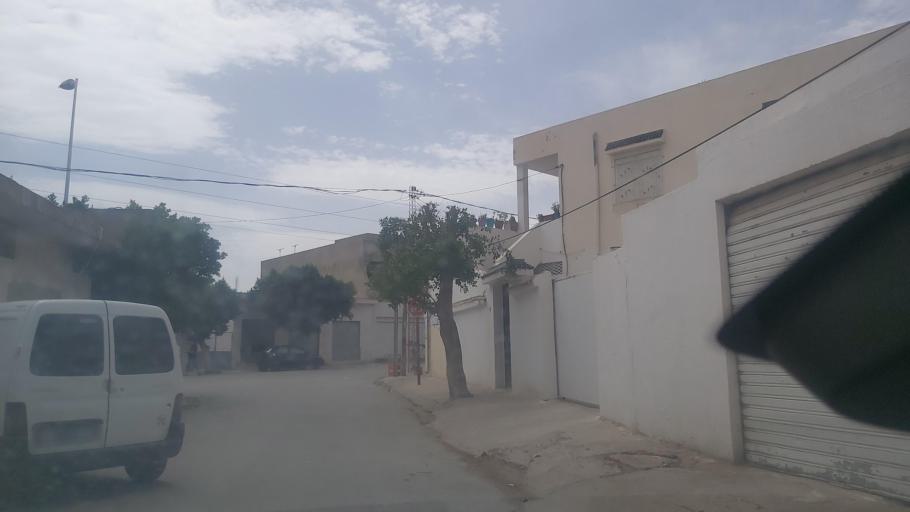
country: TN
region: Silyanah
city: Bu `Aradah
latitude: 36.3512
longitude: 9.6215
